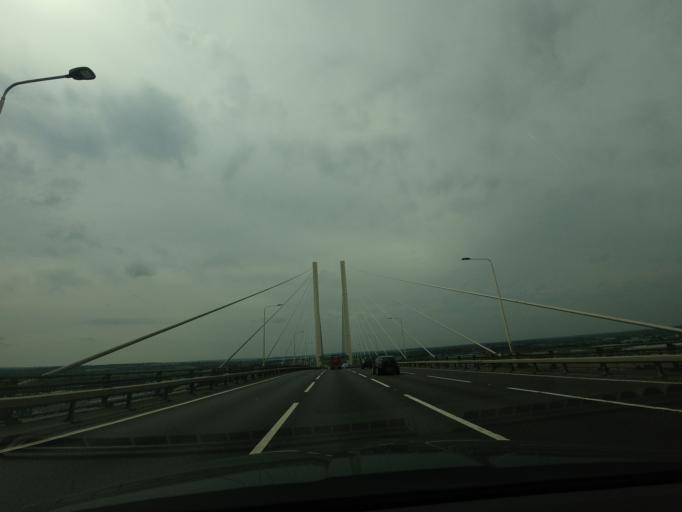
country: GB
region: England
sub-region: Kent
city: Stone
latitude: 51.4646
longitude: 0.2588
